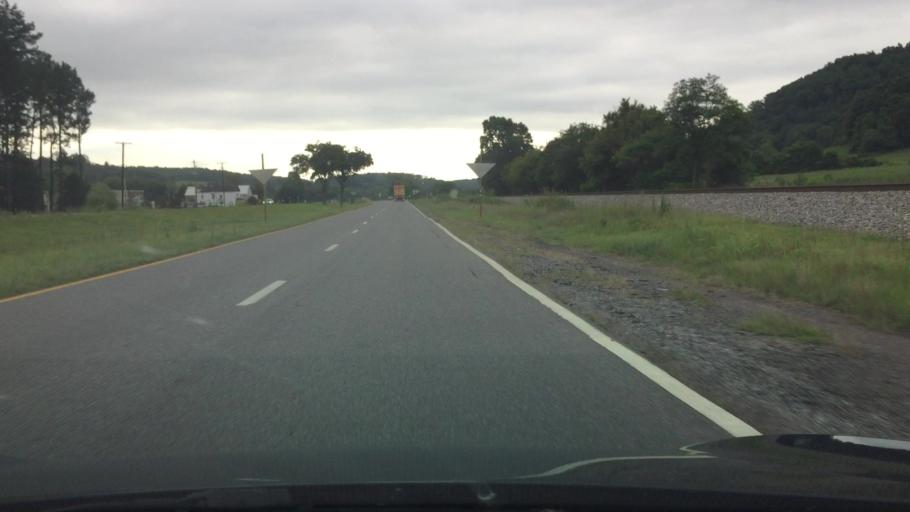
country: US
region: Virginia
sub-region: Montgomery County
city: Shawsville
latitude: 37.2293
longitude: -80.2040
